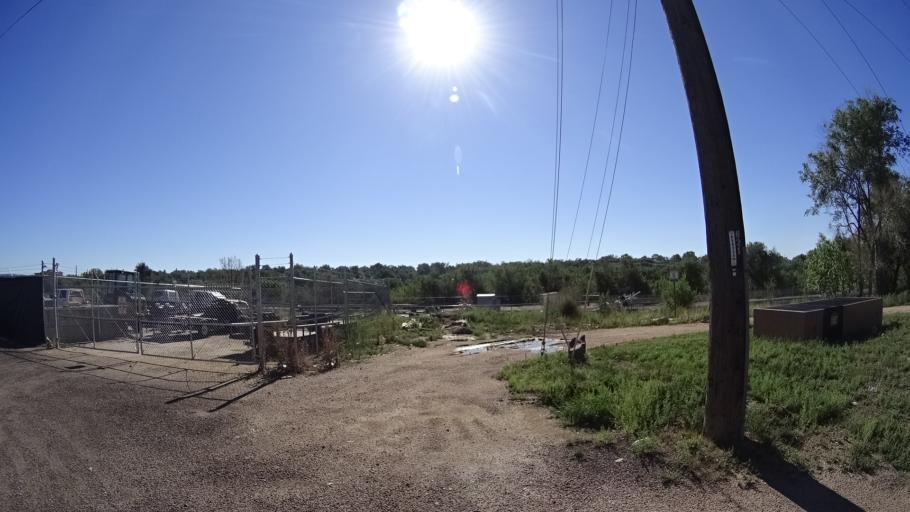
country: US
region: Colorado
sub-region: El Paso County
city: Colorado Springs
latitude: 38.8246
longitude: -104.8184
